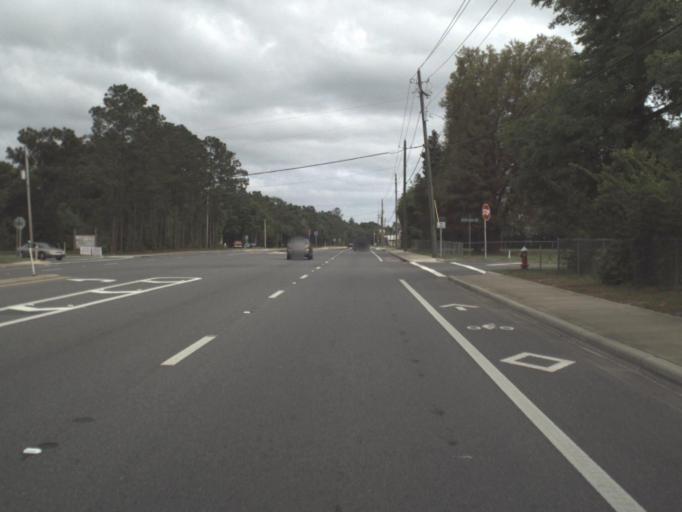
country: US
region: Florida
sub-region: Santa Rosa County
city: Point Baker
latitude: 30.6610
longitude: -87.0502
